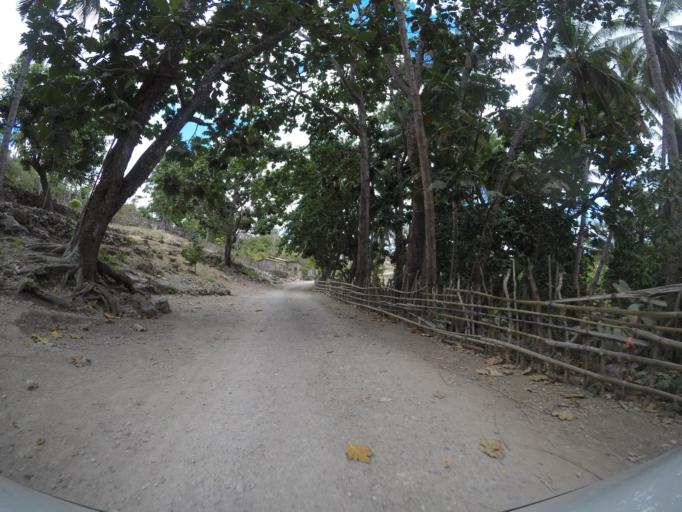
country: TL
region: Lautem
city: Lospalos
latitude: -8.3810
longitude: 126.9223
